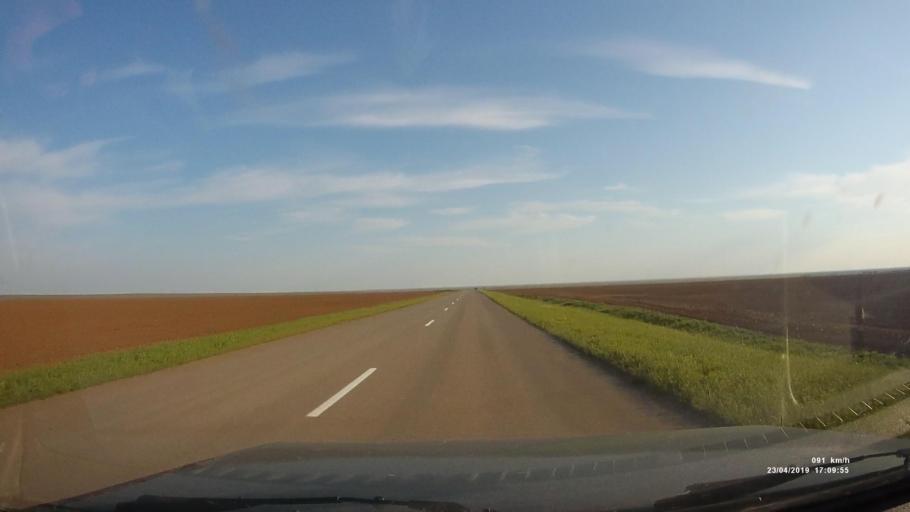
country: RU
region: Kalmykiya
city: Priyutnoye
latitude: 46.2515
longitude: 43.4842
